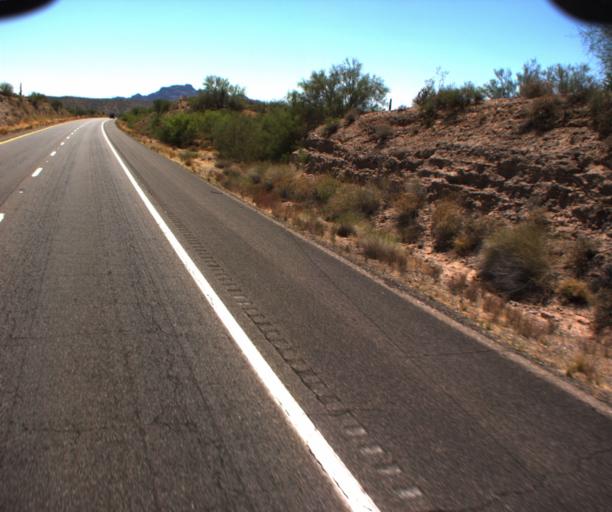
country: US
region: Arizona
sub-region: Maricopa County
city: Fountain Hills
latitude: 33.5919
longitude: -111.5969
